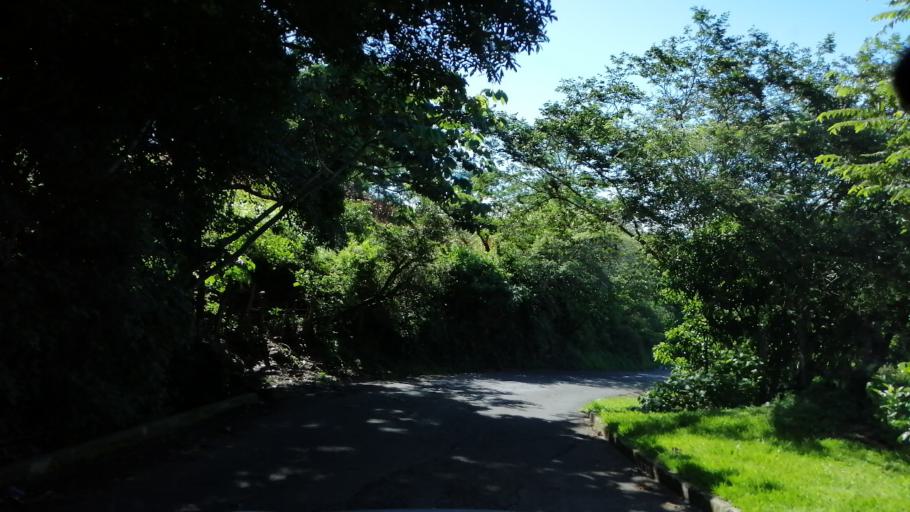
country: SV
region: Morazan
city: Corinto
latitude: 13.8116
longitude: -87.9917
